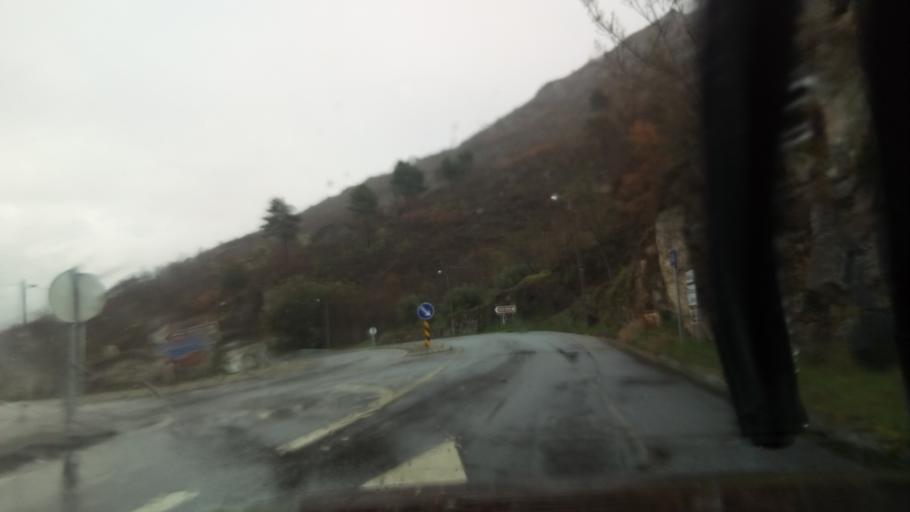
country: PT
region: Guarda
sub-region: Guarda
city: Guarda
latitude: 40.5694
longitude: -7.2979
